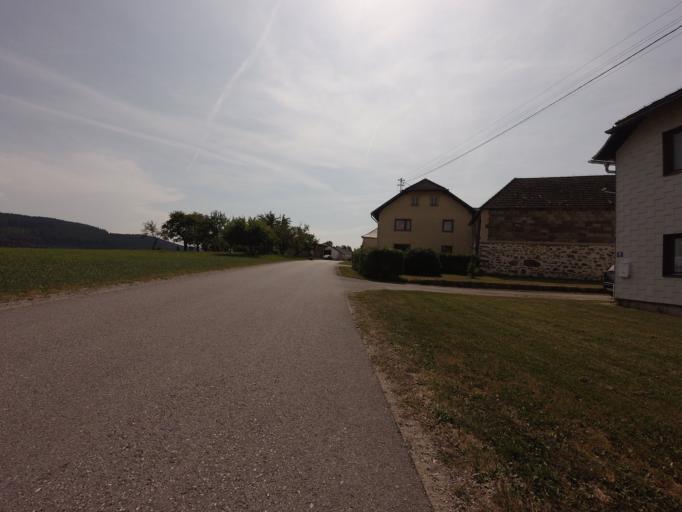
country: AT
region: Upper Austria
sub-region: Politischer Bezirk Urfahr-Umgebung
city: Reichenthal
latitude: 48.5301
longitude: 14.3617
